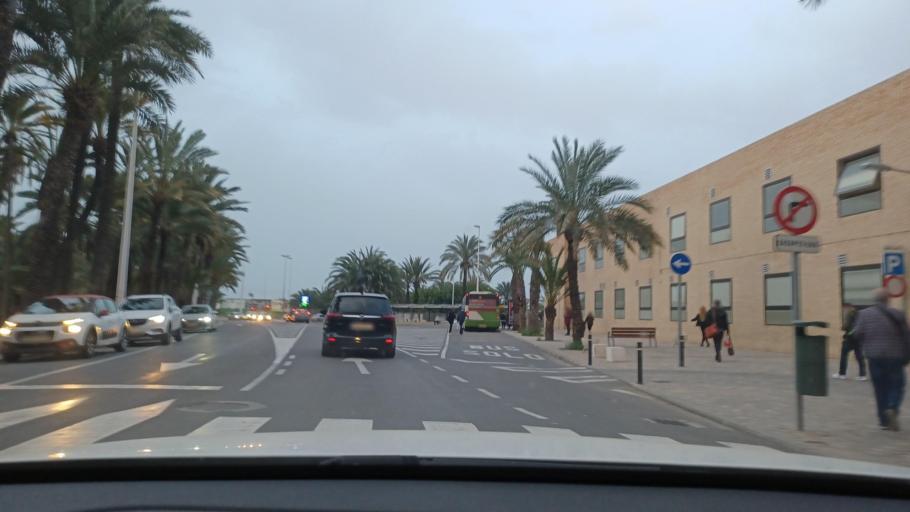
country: ES
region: Valencia
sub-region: Provincia de Alicante
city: Elche
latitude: 38.2602
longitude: -0.6840
